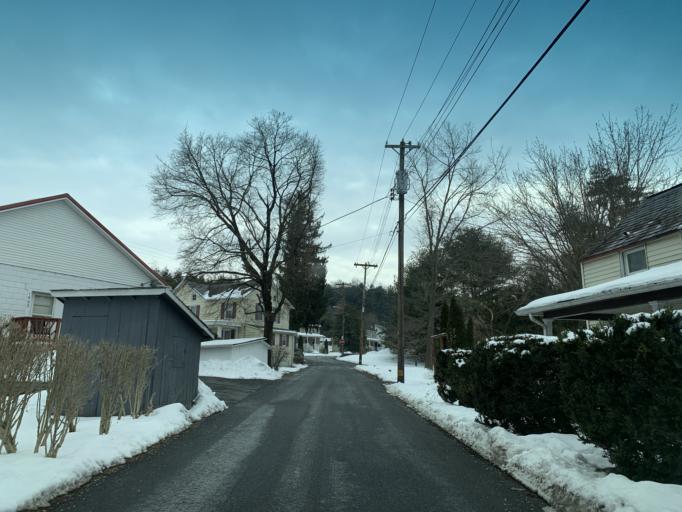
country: US
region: Pennsylvania
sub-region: York County
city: Susquehanna Trails
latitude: 39.7182
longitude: -76.3383
